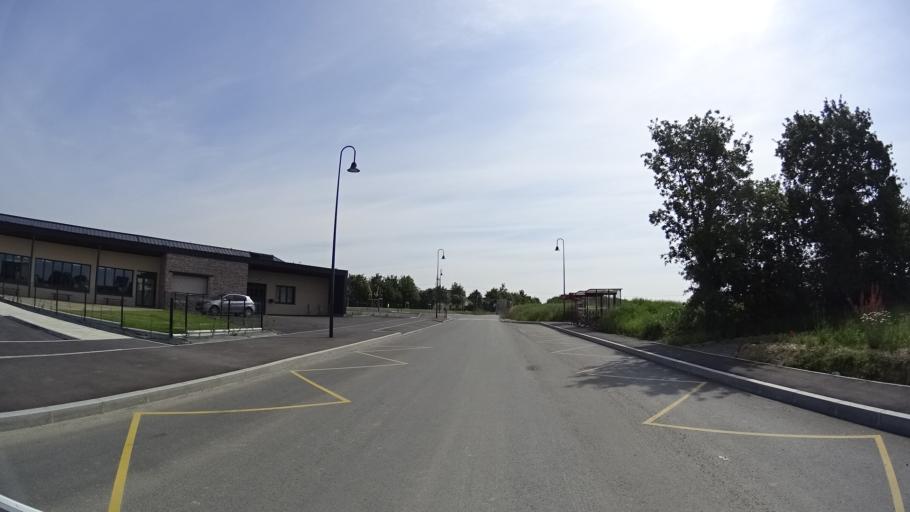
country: FR
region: Brittany
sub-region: Departement d'Ille-et-Vilaine
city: Nouvoitou
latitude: 48.0397
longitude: -1.5411
